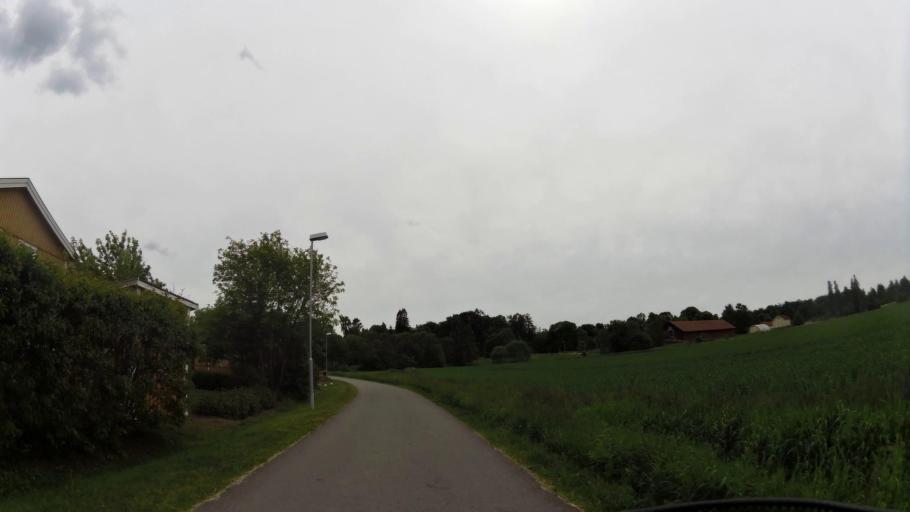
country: SE
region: OEstergoetland
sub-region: Linkopings Kommun
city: Malmslatt
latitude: 58.3807
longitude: 15.5625
